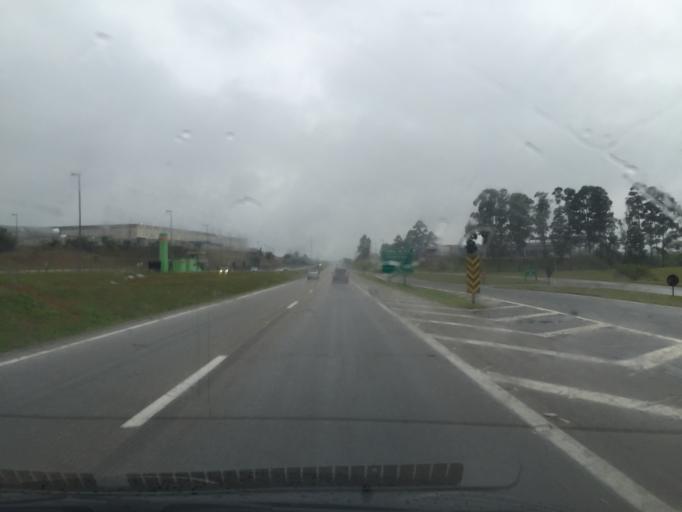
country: BR
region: Sao Paulo
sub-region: Itu
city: Itu
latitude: -23.3630
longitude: -47.3263
